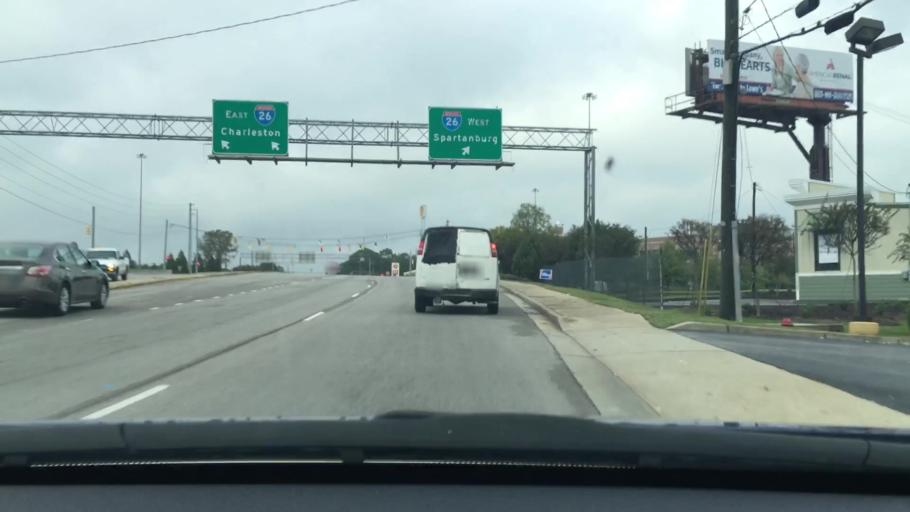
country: US
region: South Carolina
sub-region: Lexington County
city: West Columbia
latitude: 34.0036
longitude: -81.1085
